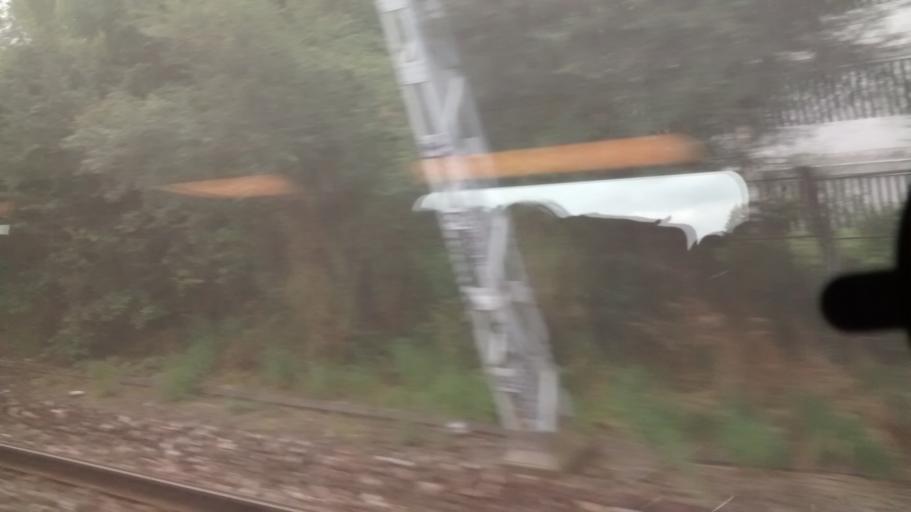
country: FR
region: Ile-de-France
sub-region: Departement du Val-de-Marne
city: Fresnes
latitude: 48.7473
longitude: 2.3160
